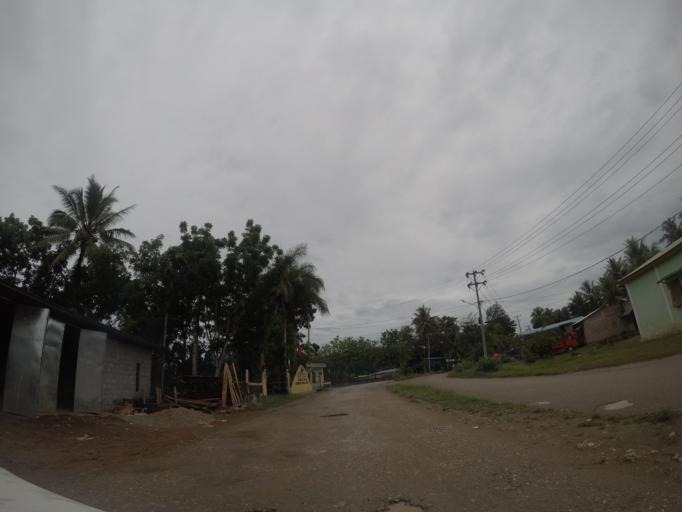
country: TL
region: Lautem
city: Lospalos
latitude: -8.5132
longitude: 127.0042
